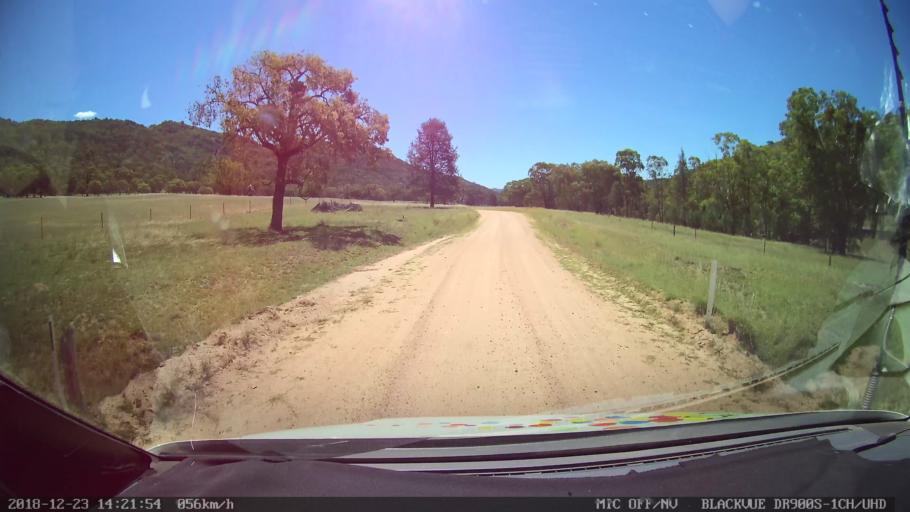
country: AU
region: New South Wales
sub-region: Tamworth Municipality
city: Manilla
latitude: -30.6445
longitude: 150.9772
